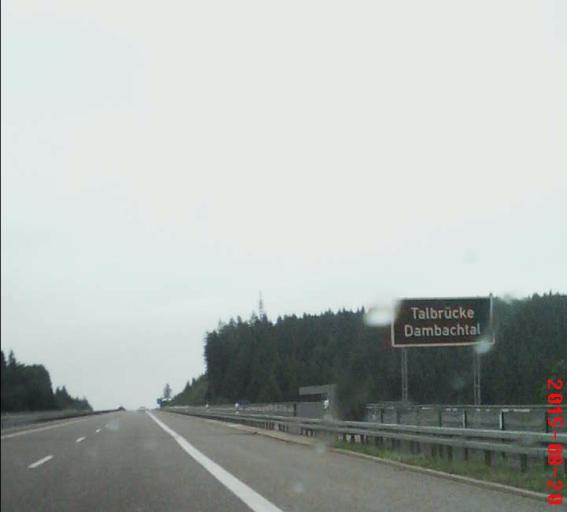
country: DE
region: Thuringia
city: Suhl
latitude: 50.5709
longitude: 10.7293
